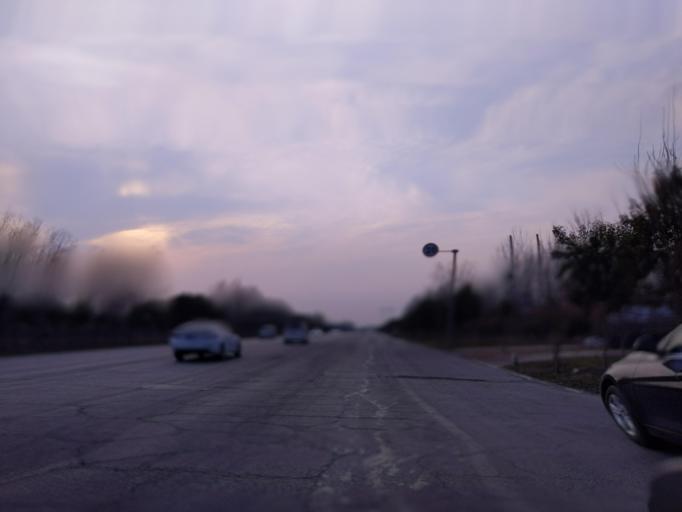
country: CN
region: Henan Sheng
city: Puyang
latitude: 35.8195
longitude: 114.9912
